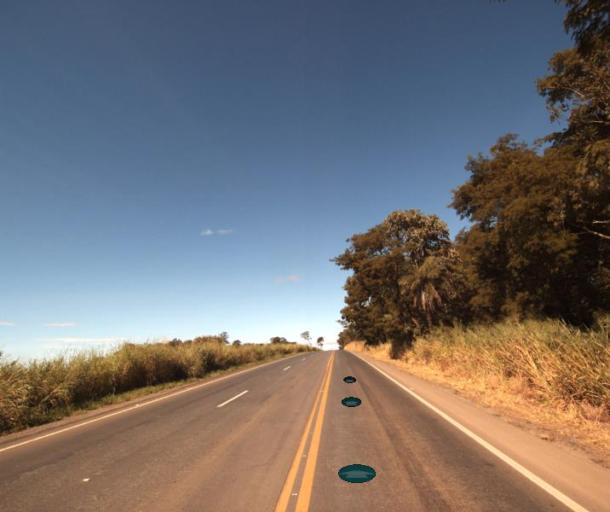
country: BR
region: Goias
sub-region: Itapaci
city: Itapaci
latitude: -14.9889
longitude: -49.4035
